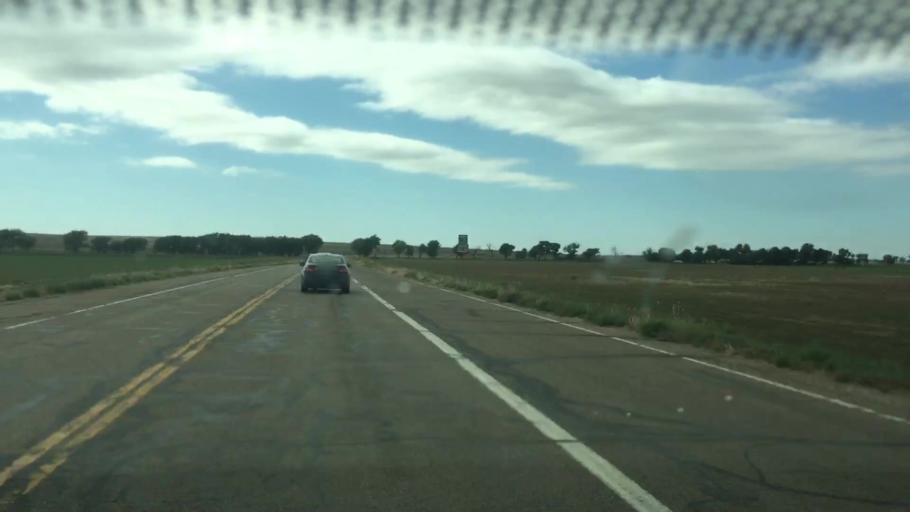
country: US
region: Colorado
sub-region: Prowers County
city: Lamar
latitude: 38.0640
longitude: -102.3465
